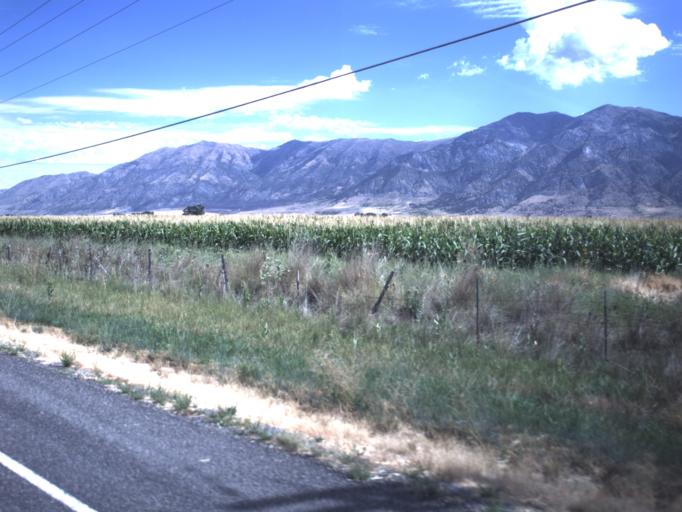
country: US
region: Utah
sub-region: Box Elder County
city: Honeyville
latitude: 41.5692
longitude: -112.1296
